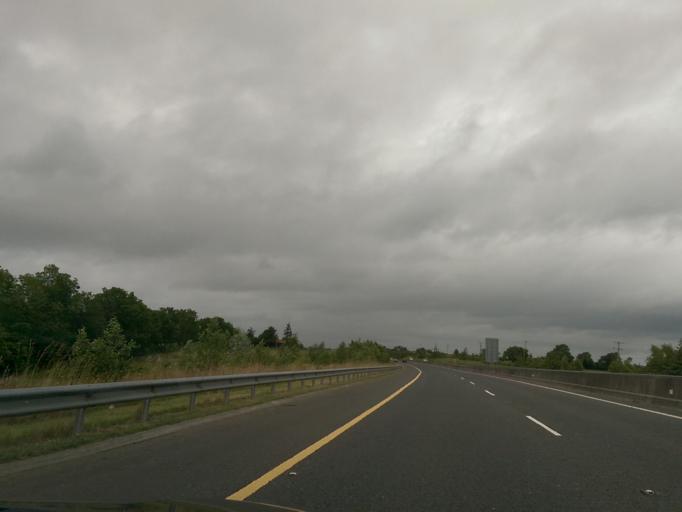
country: IE
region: Munster
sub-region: An Clar
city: Newmarket on Fergus
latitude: 52.7963
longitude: -8.9218
